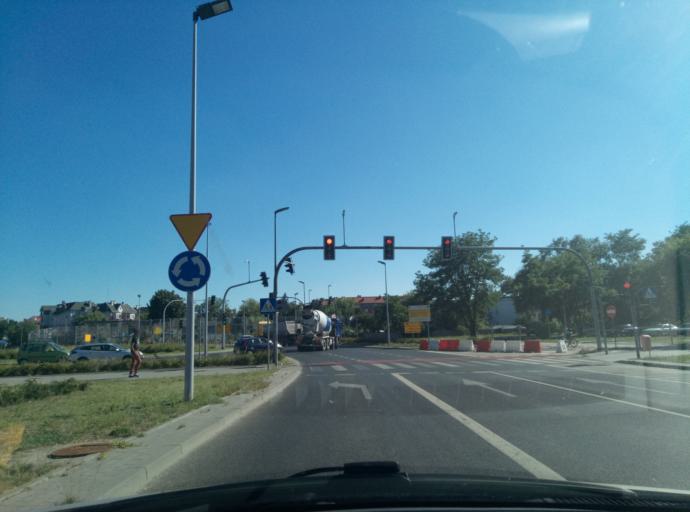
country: PL
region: Kujawsko-Pomorskie
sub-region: Torun
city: Torun
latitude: 53.0254
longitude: 18.5914
